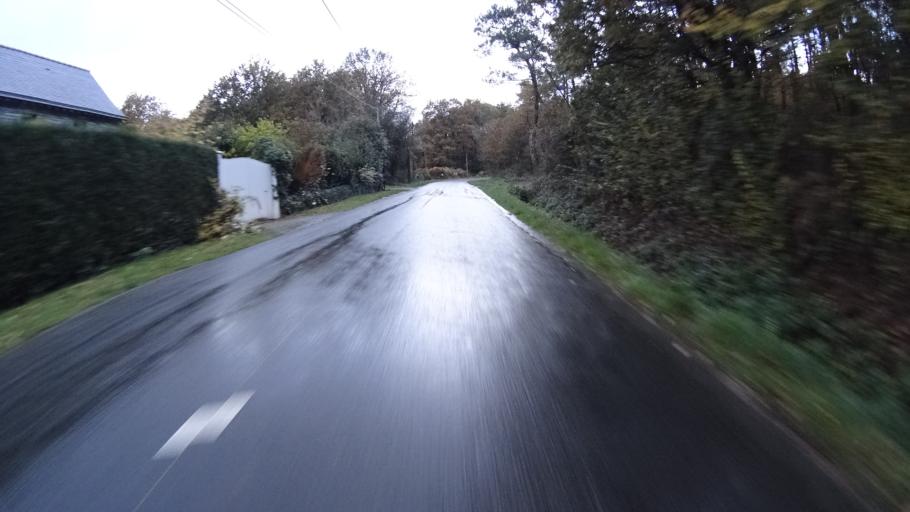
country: FR
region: Brittany
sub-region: Departement d'Ille-et-Vilaine
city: Sainte-Marie
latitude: 47.6835
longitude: -1.9965
